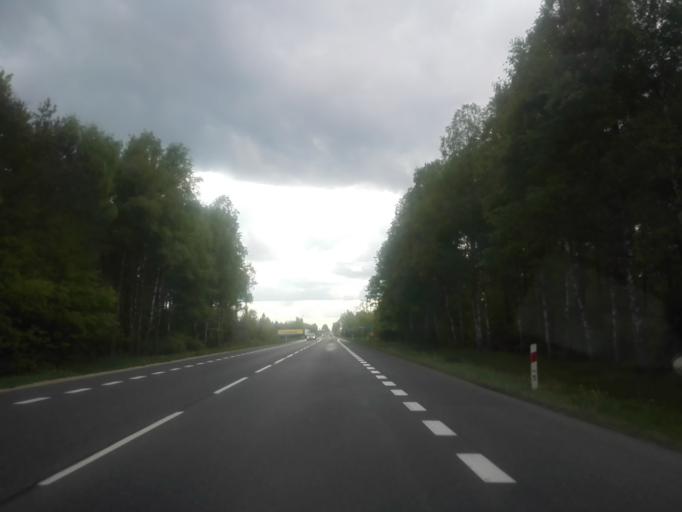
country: PL
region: Masovian Voivodeship
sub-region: Powiat ostrowski
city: Ostrow Mazowiecka
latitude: 52.8294
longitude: 21.9415
